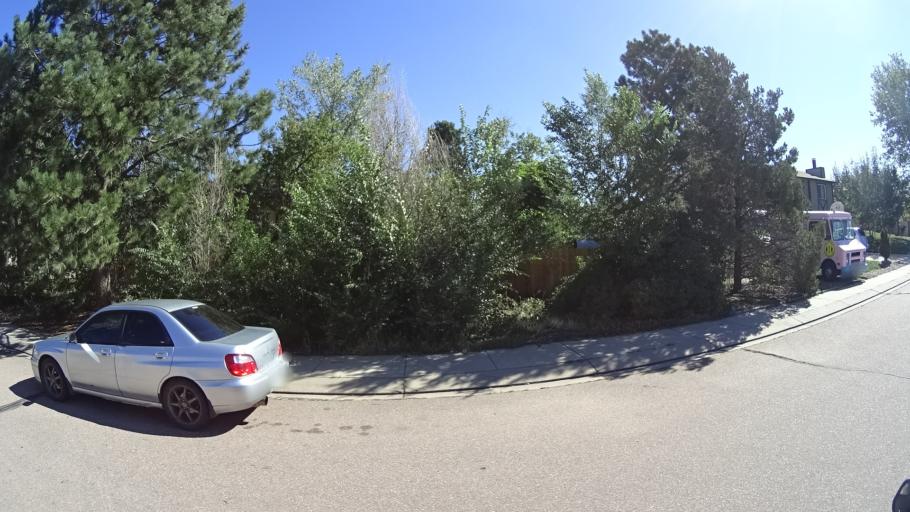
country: US
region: Colorado
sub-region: El Paso County
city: Cimarron Hills
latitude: 38.8177
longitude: -104.7354
